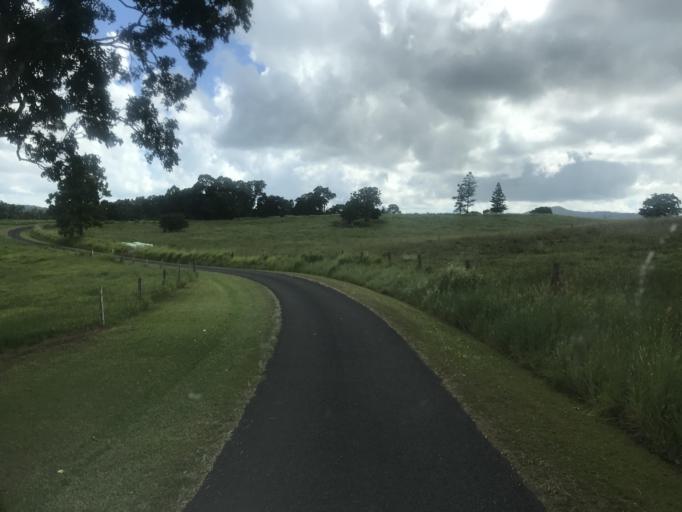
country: AU
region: Queensland
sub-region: Tablelands
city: Ravenshoe
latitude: -17.5554
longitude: 145.6907
